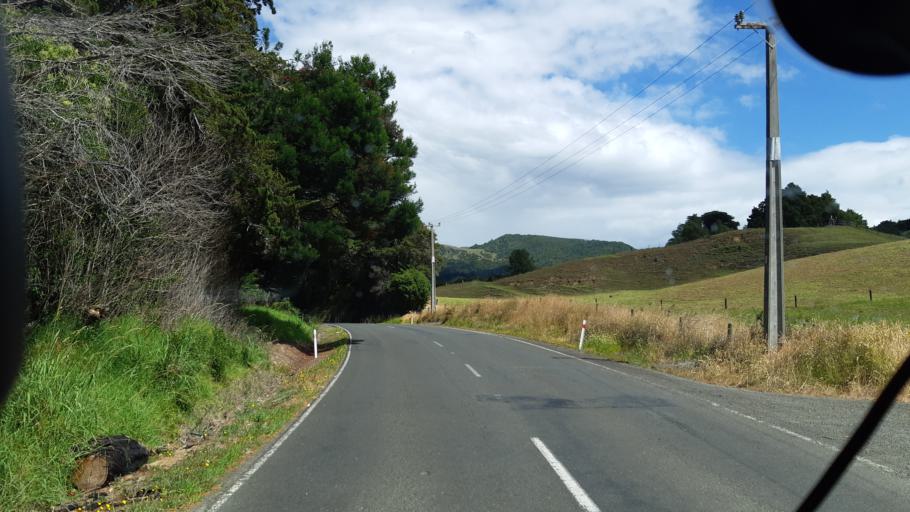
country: NZ
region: Northland
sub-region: Far North District
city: Taipa
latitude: -35.2745
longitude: 173.5171
